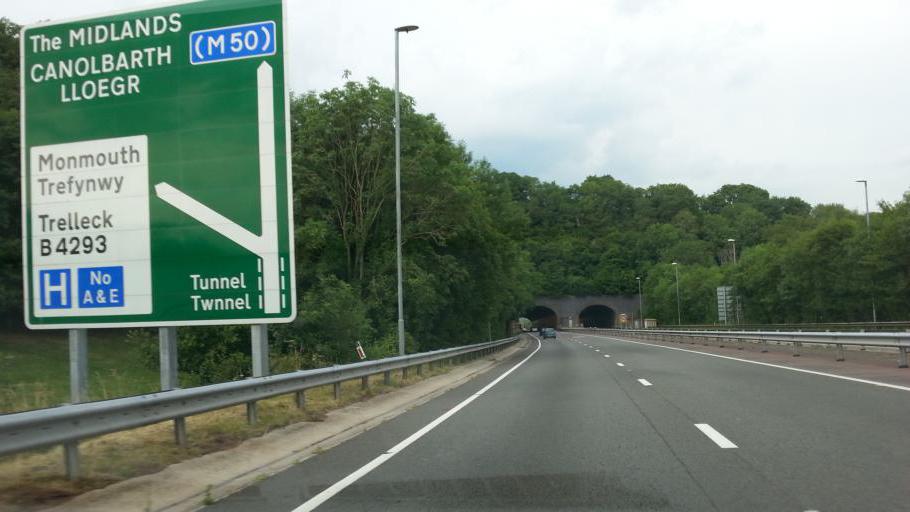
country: GB
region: Wales
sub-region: Monmouthshire
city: Monmouth
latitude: 51.8009
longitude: -2.7203
